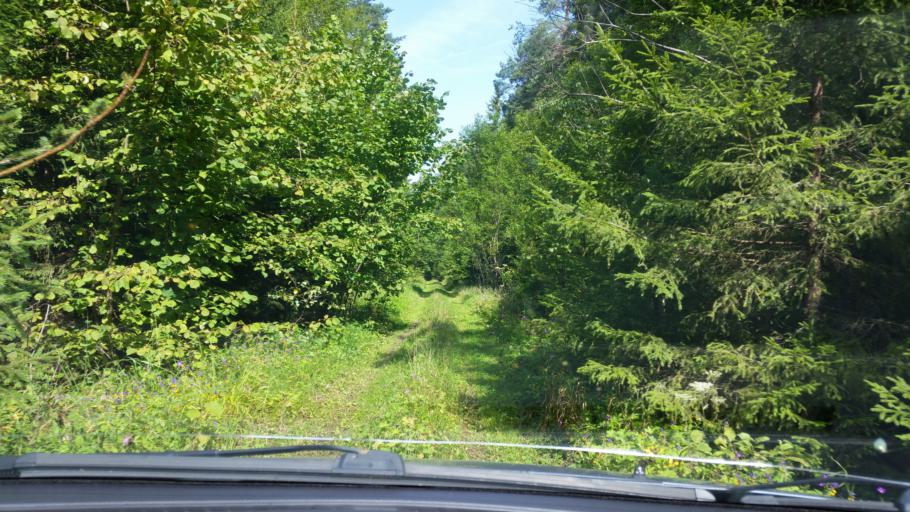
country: RU
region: Moskovskaya
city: Bol'shoye Gryzlovo
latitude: 54.9131
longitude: 37.7547
